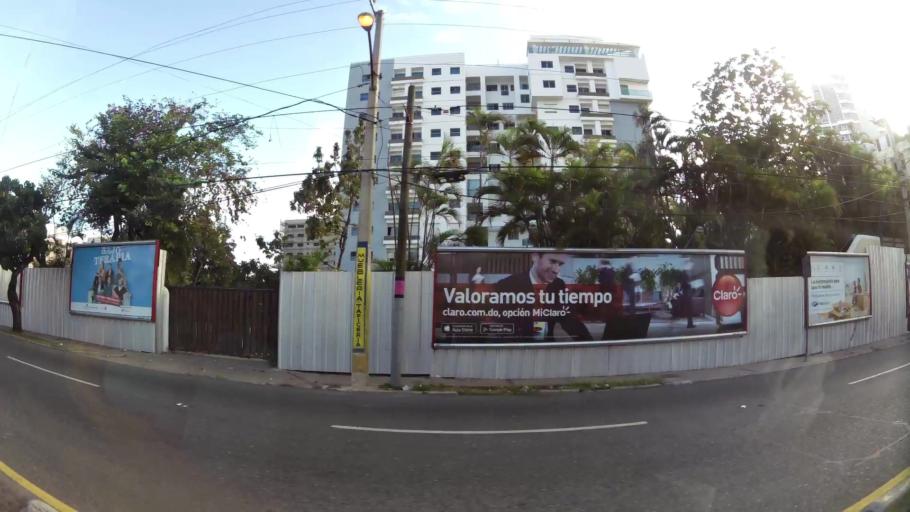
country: DO
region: Nacional
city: La Julia
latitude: 18.4681
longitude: -69.9227
